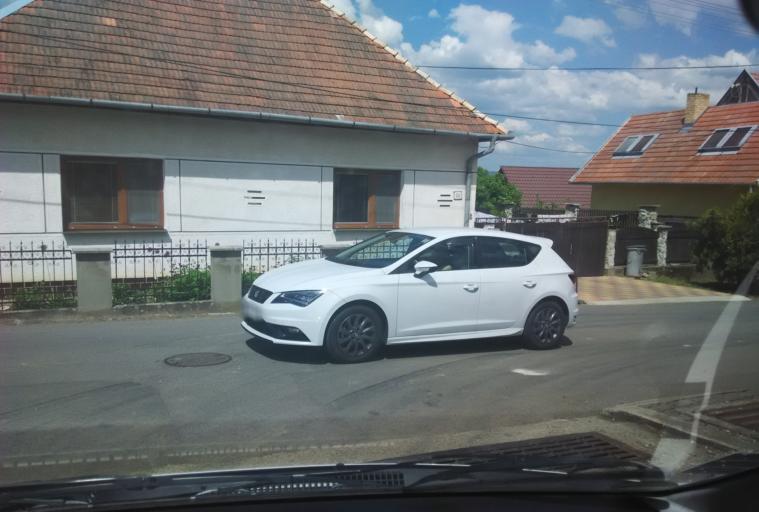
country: SK
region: Banskobystricky
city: Dudince
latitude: 48.1652
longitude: 18.8956
